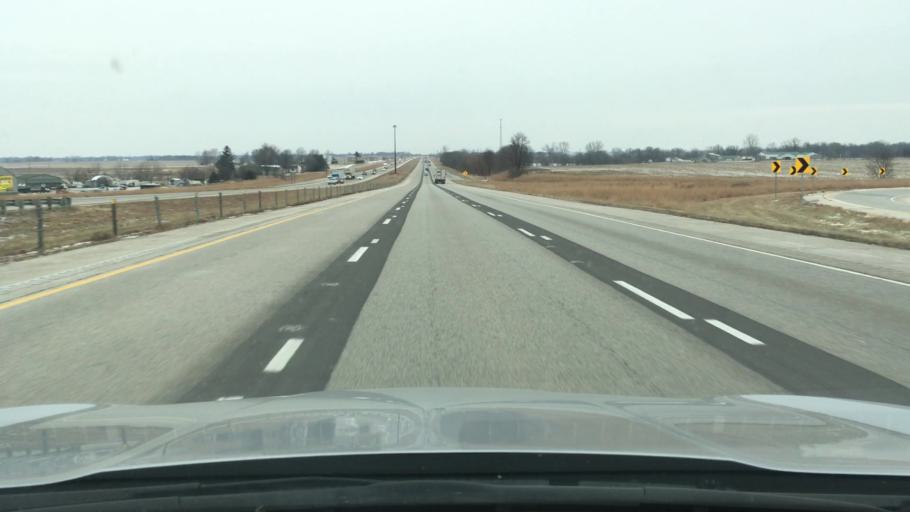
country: US
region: Illinois
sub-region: Sangamon County
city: Divernon
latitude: 39.5916
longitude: -89.6464
